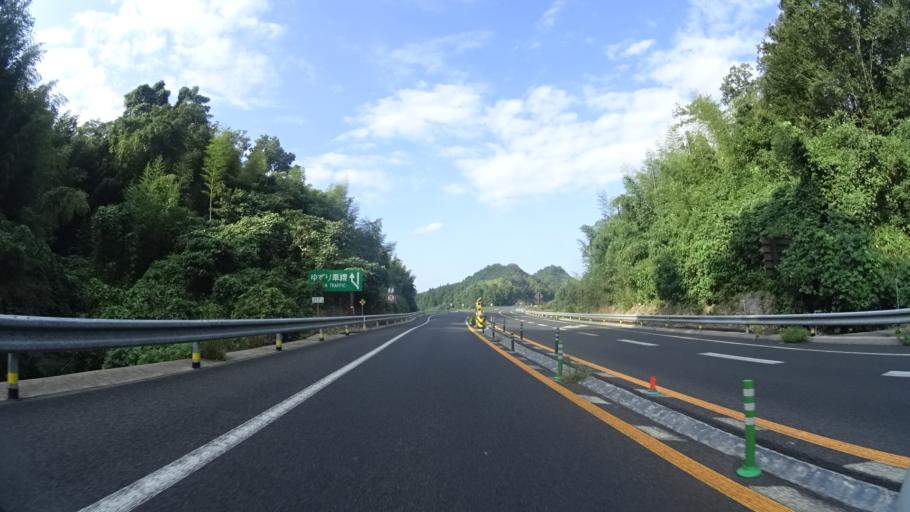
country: JP
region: Shimane
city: Izumo
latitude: 35.3407
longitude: 132.8145
